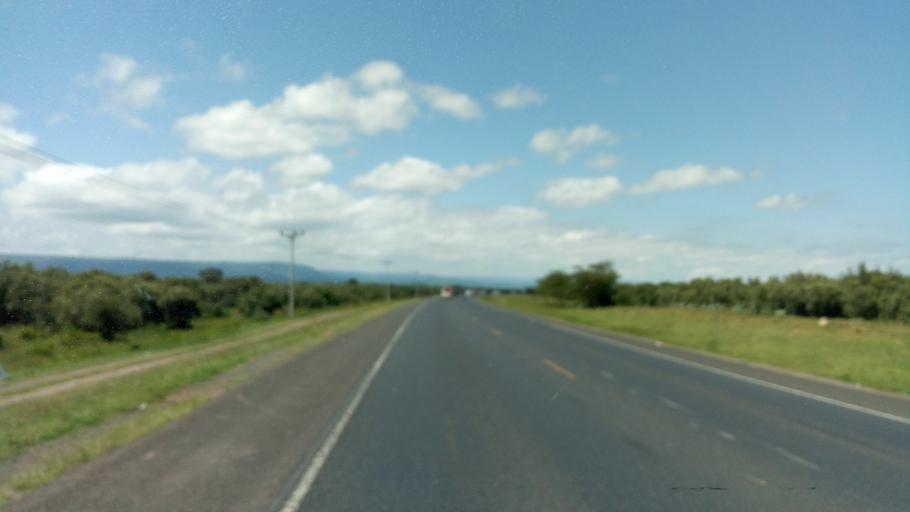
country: KE
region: Nakuru
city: Naivasha
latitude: -0.5467
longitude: 36.3442
